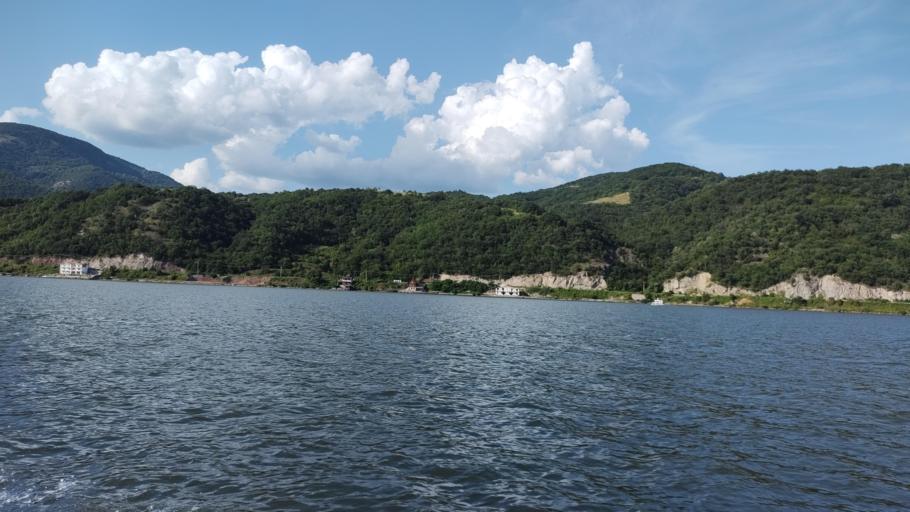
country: RO
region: Mehedinti
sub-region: Comuna Svinita
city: Svinita
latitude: 44.5305
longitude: 22.0678
